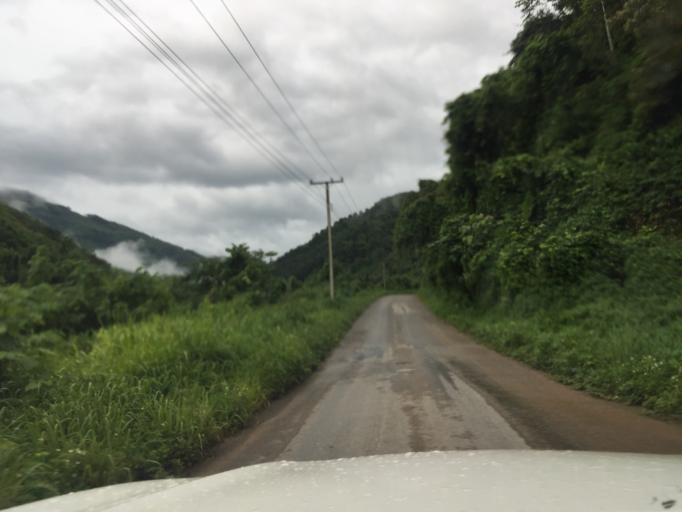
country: LA
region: Oudomxai
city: Muang La
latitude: 21.0190
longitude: 102.2326
